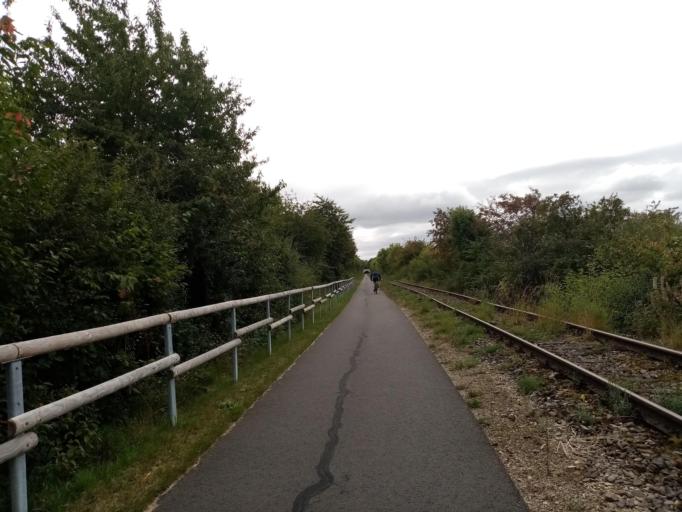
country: DE
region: Thuringia
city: Dingelstadt
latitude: 51.3039
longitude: 10.3049
